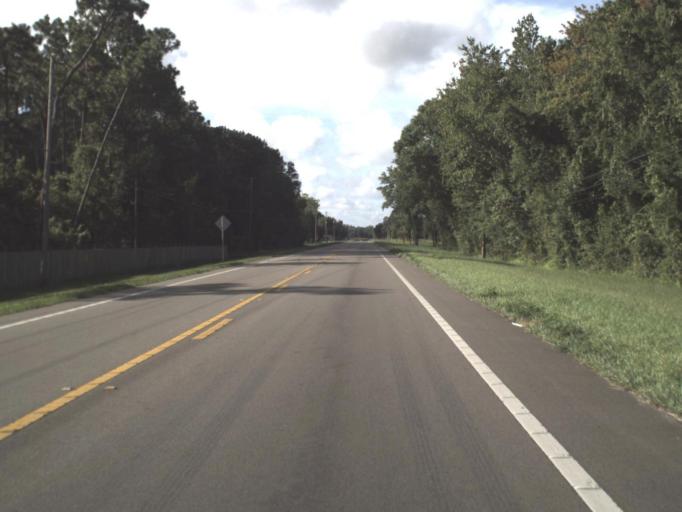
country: US
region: Florida
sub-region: Pasco County
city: Shady Hills
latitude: 28.3510
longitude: -82.5043
